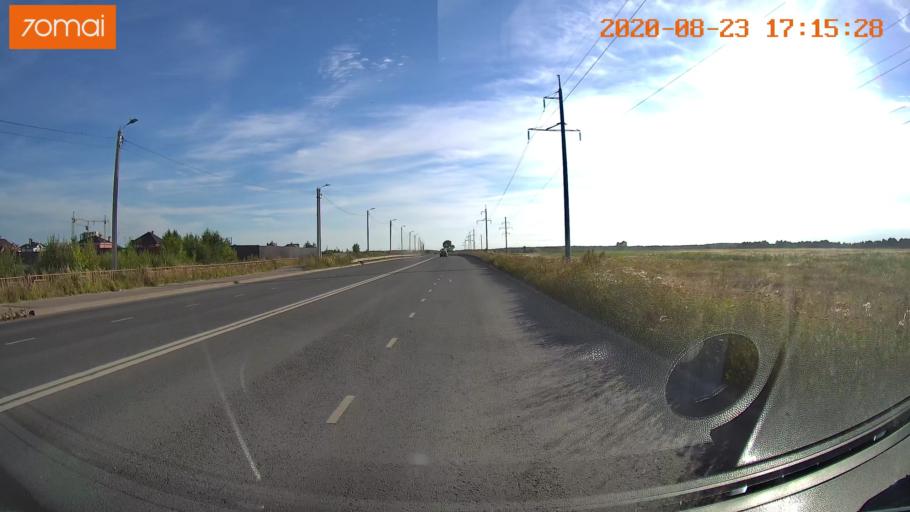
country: RU
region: Ivanovo
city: Novo-Talitsy
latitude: 57.0452
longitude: 40.9125
